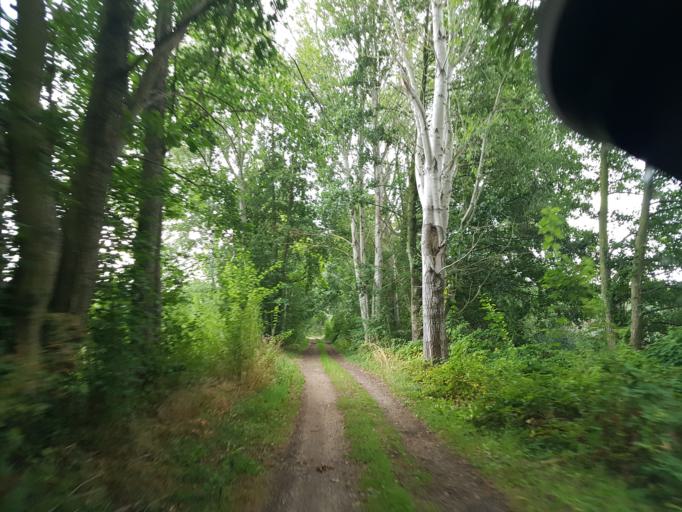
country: DE
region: Brandenburg
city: Ruckersdorf
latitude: 51.6008
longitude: 13.5695
